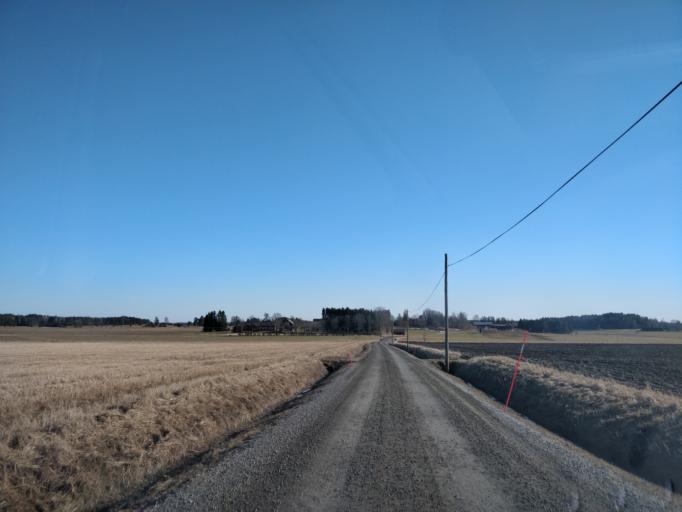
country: SE
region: Uppsala
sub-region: Enkopings Kommun
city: Enkoping
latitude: 59.8189
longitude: 17.1223
